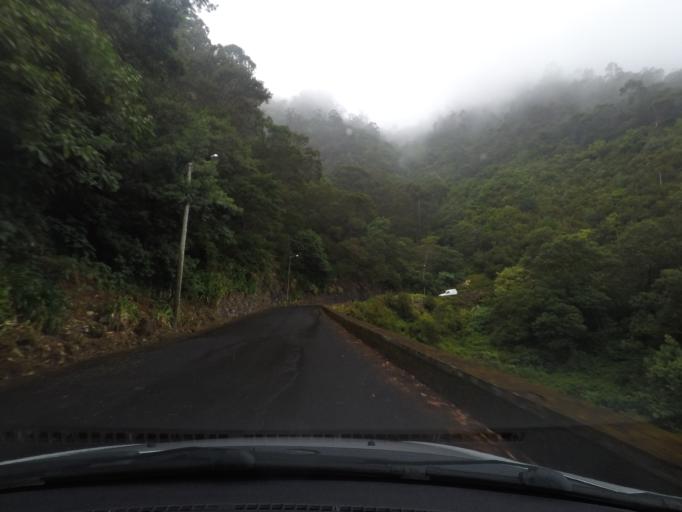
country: PT
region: Madeira
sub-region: Santana
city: Santana
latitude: 32.7872
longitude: -16.8609
